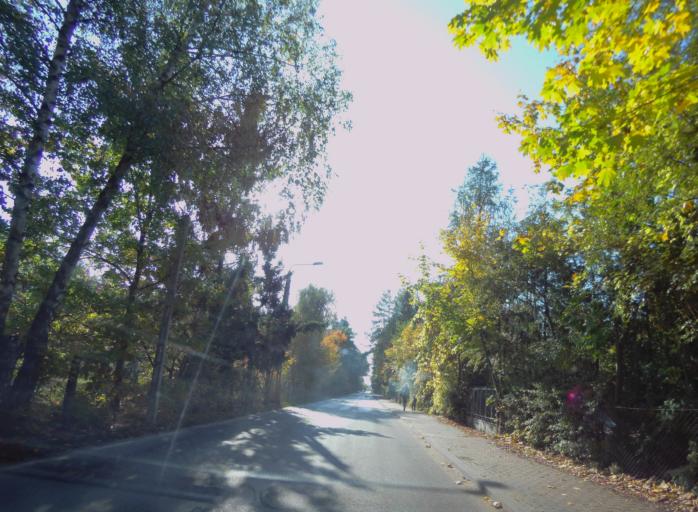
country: PL
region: Masovian Voivodeship
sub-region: Powiat otwocki
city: Jozefow
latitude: 52.1711
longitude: 21.3014
